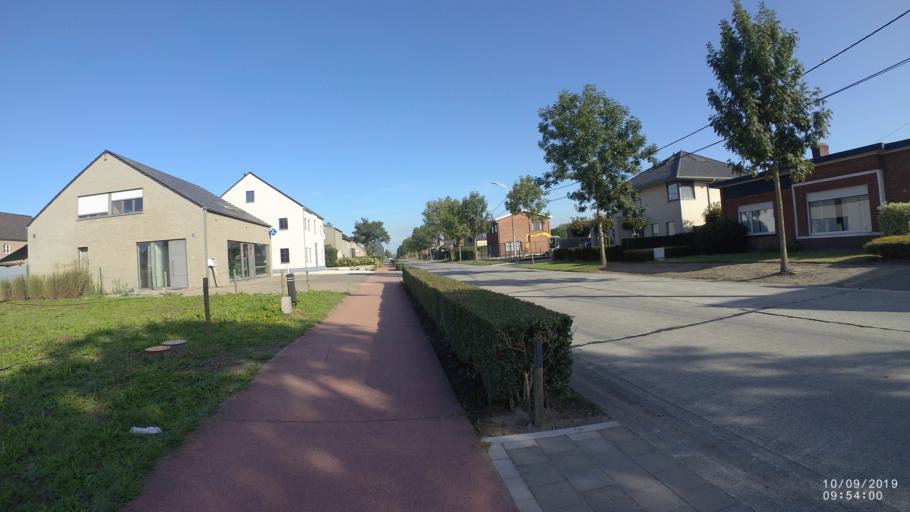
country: BE
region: Flanders
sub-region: Provincie Oost-Vlaanderen
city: Lochristi
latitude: 51.1018
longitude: 3.8424
